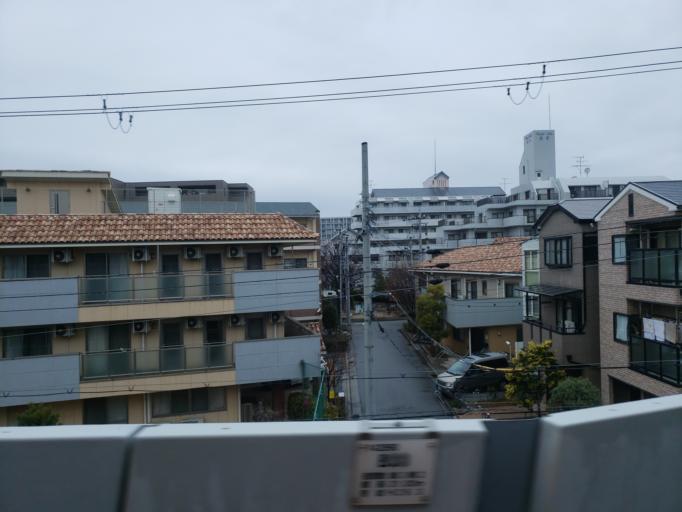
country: JP
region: Hyogo
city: Amagasaki
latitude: 34.7193
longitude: 135.3761
